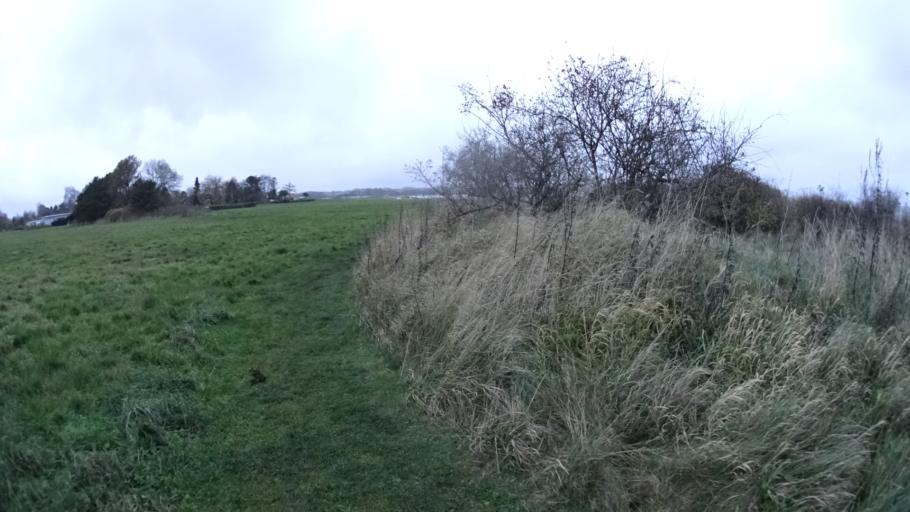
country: DK
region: Central Jutland
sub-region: Arhus Kommune
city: Beder
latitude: 56.0208
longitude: 10.2810
